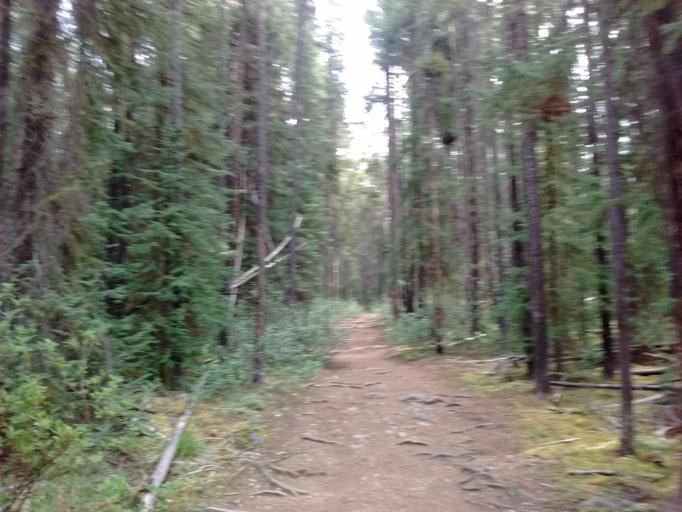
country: CA
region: Alberta
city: Jasper Park Lodge
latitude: 52.5260
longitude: -117.6555
